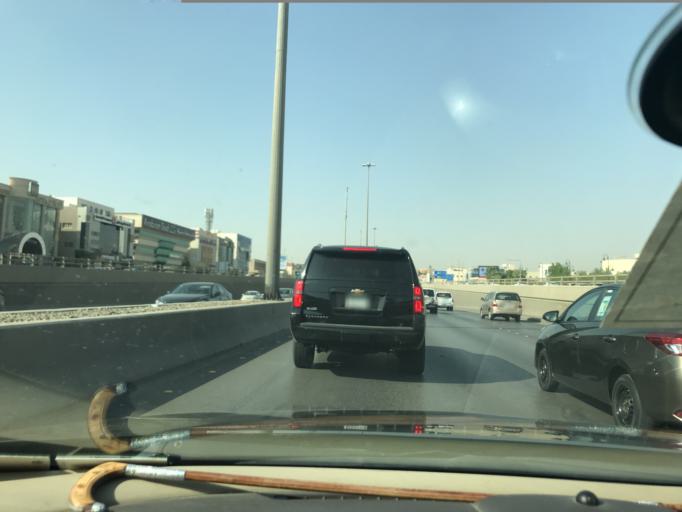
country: SA
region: Ar Riyad
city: Riyadh
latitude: 24.6845
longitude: 46.7022
